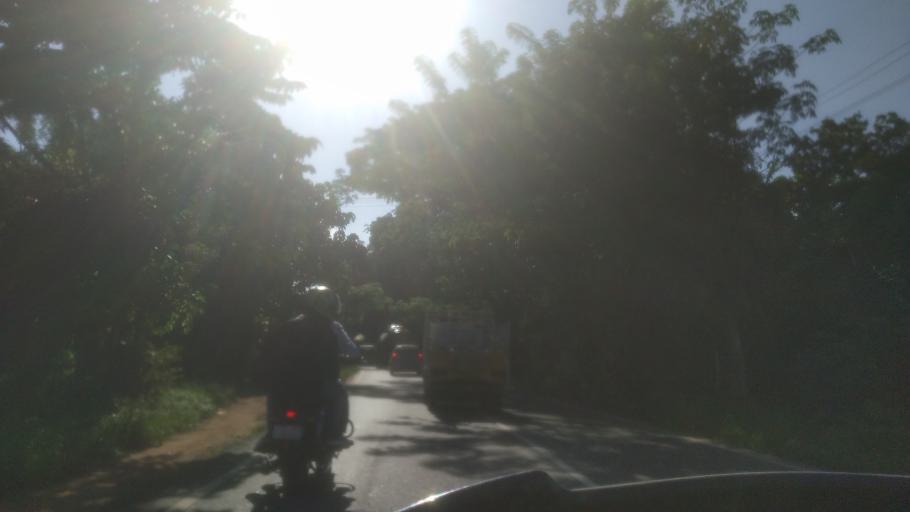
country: IN
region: Kerala
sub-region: Ernakulam
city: Ramamangalam
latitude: 9.9765
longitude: 76.5058
